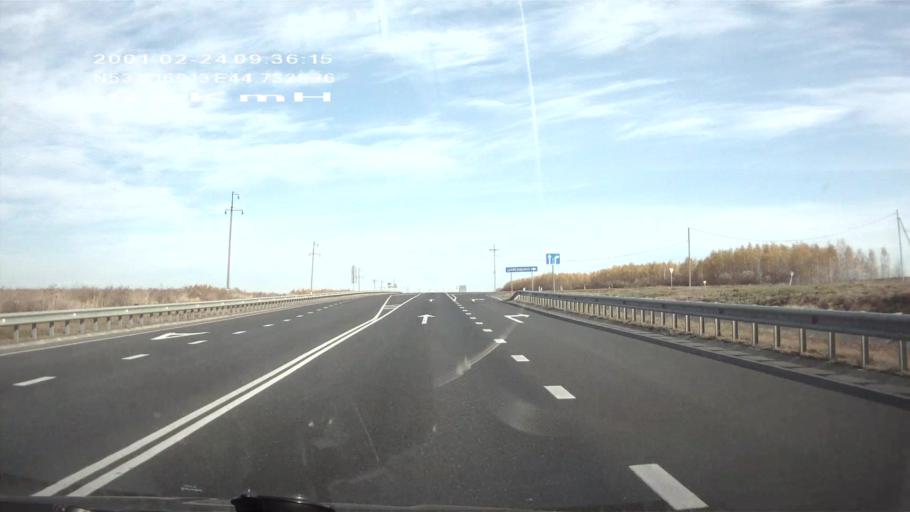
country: RU
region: Penza
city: Mokshan
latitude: 53.6160
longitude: 44.7330
